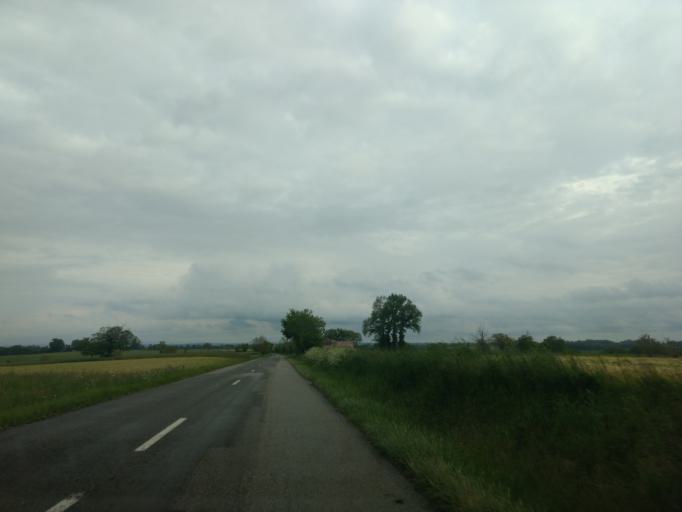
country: FR
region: Midi-Pyrenees
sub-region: Departement de l'Aveyron
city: Viviez
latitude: 44.5296
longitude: 2.1760
